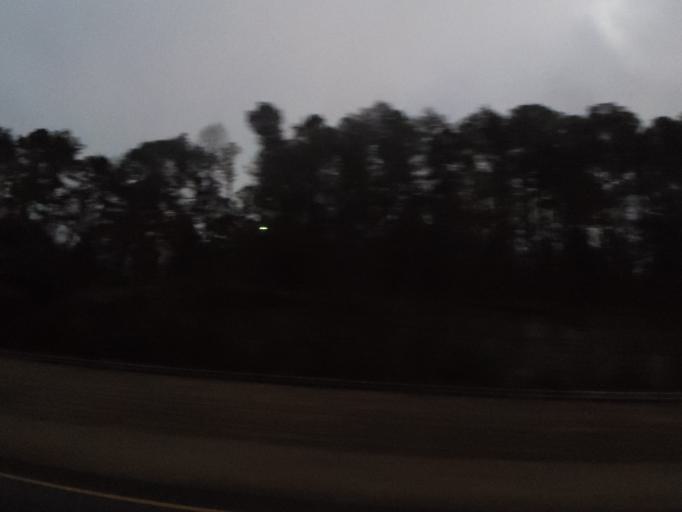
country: US
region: Alabama
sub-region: Morgan County
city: Falkville
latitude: 34.2887
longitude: -86.9100
